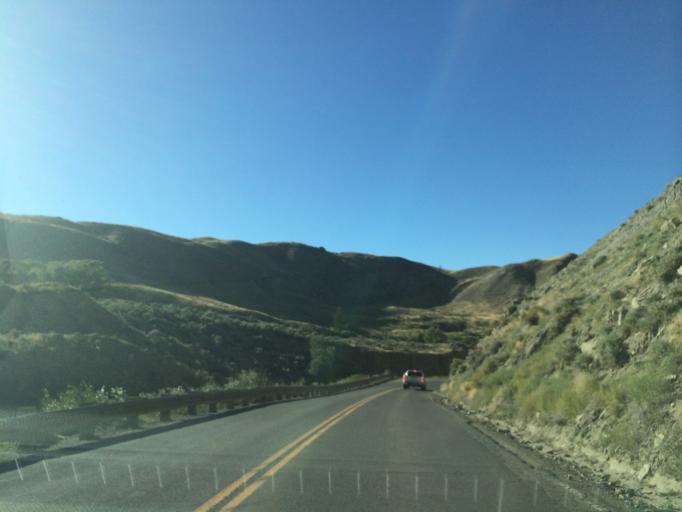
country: US
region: Montana
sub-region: Gallatin County
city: West Yellowstone
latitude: 45.0056
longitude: -110.6927
